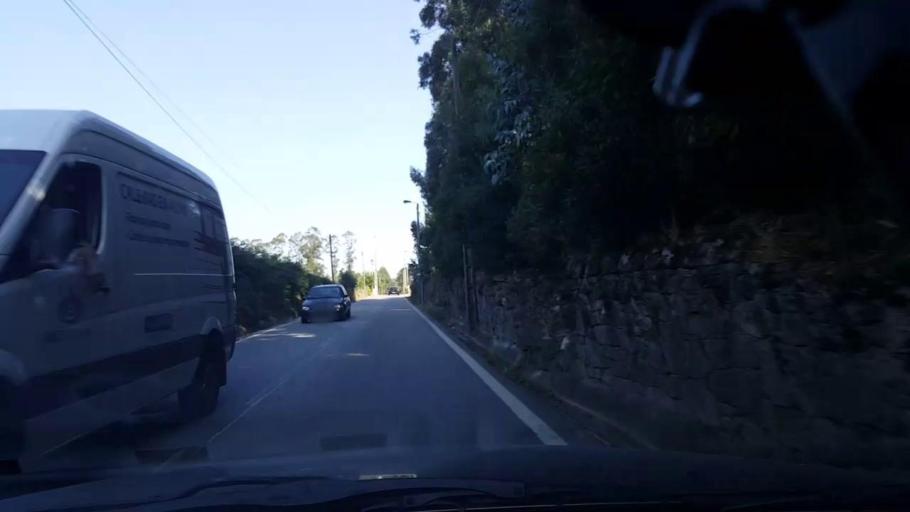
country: PT
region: Porto
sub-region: Vila do Conde
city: Arvore
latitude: 41.3171
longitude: -8.6792
